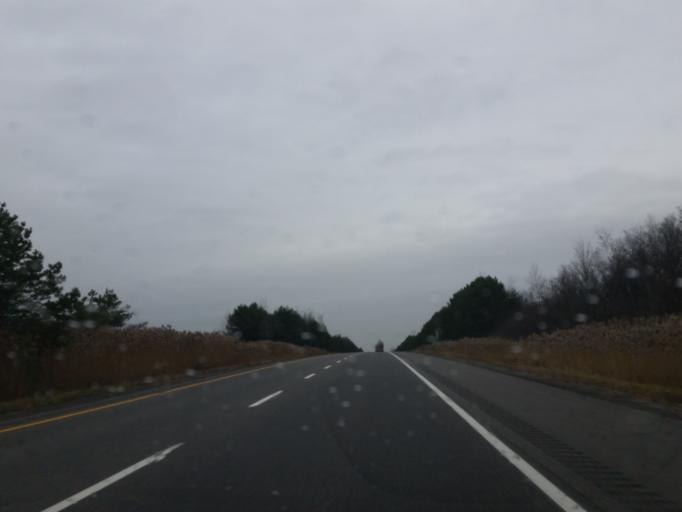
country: CA
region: Quebec
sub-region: Mauricie
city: Becancour
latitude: 46.5262
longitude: -72.2838
